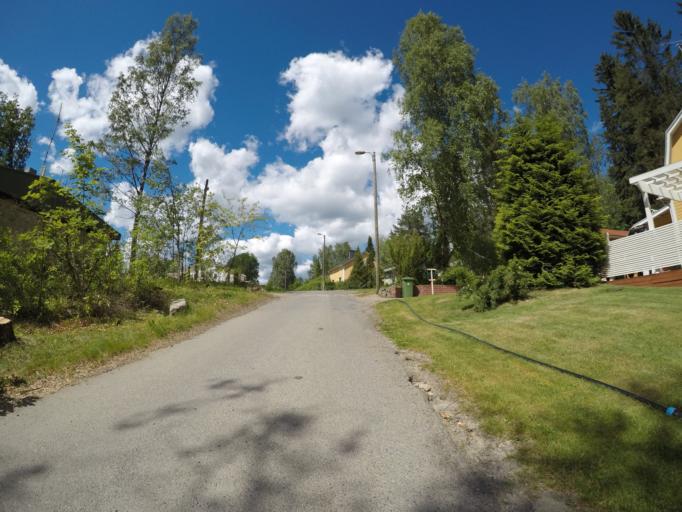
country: FI
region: Haeme
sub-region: Haemeenlinna
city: Haemeenlinna
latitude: 61.0080
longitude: 24.4415
